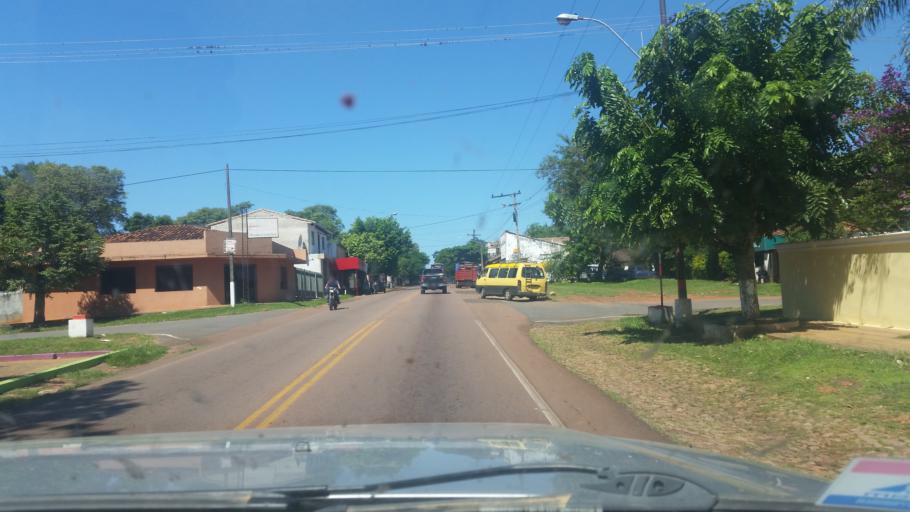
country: PY
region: Paraguari
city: Quiindy
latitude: -25.8786
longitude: -57.2897
